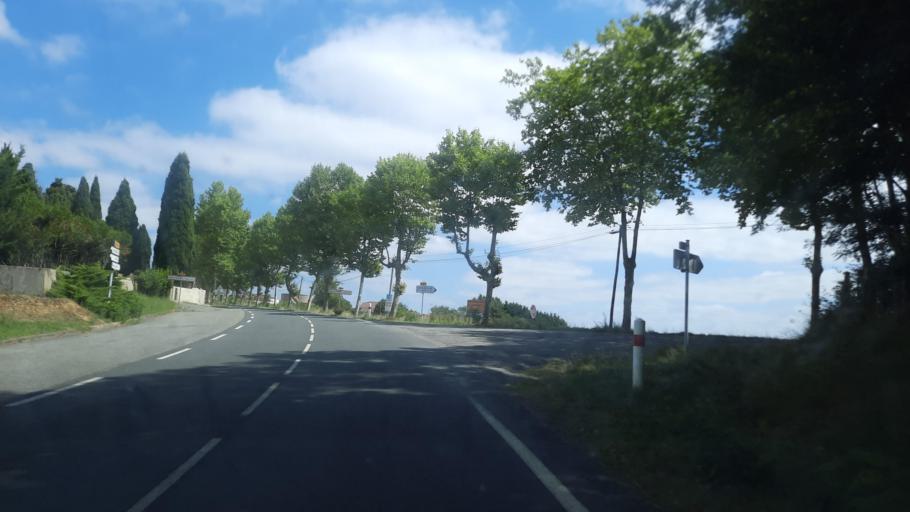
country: FR
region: Midi-Pyrenees
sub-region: Departement de la Haute-Garonne
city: Boulogne-sur-Gesse
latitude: 43.2891
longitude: 0.6388
